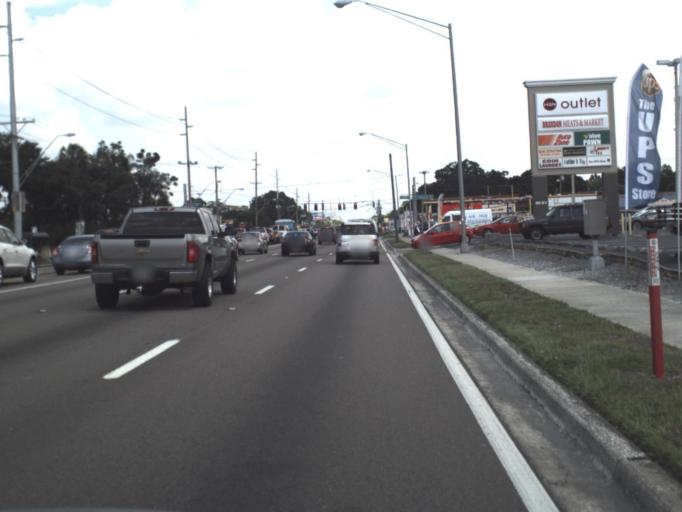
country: US
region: Florida
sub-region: Hillsborough County
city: Brandon
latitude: 27.9376
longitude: -82.2878
